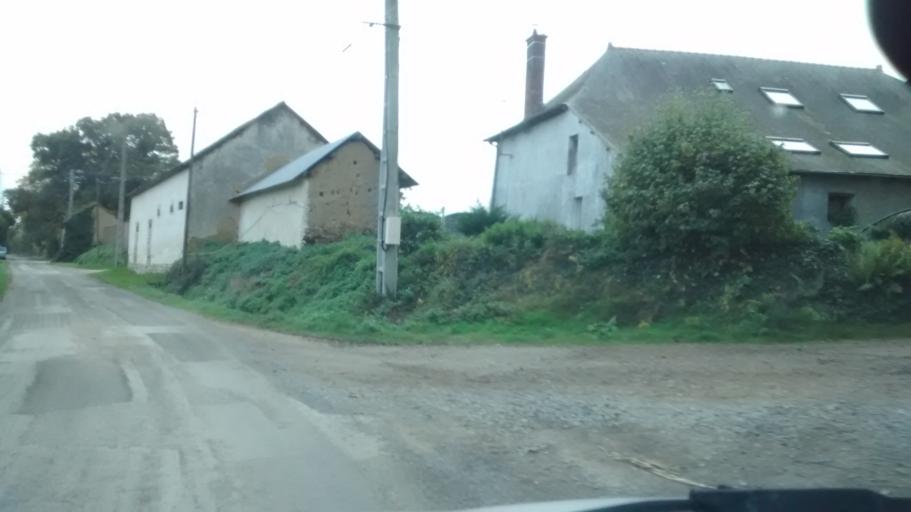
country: FR
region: Brittany
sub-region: Departement d'Ille-et-Vilaine
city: Acigne
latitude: 48.1629
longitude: -1.5209
